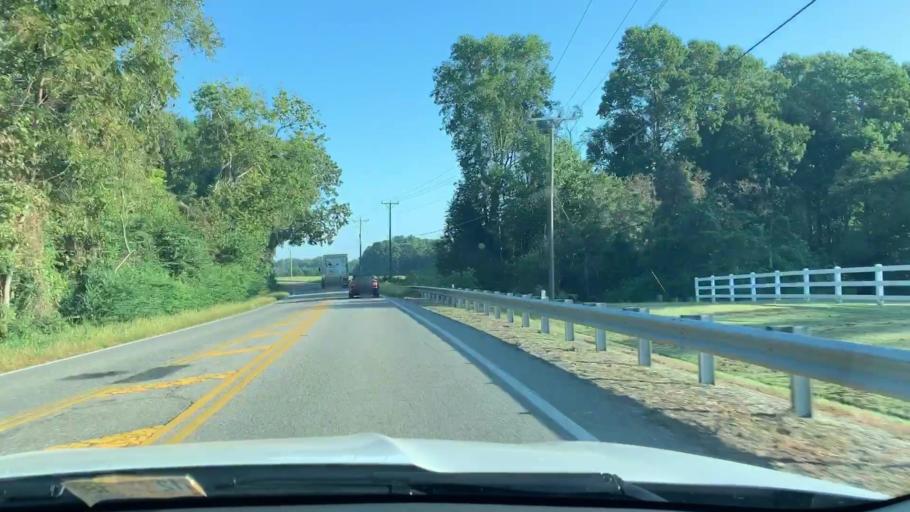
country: US
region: Virginia
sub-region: Middlesex County
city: Deltaville
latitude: 37.5292
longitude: -76.4218
